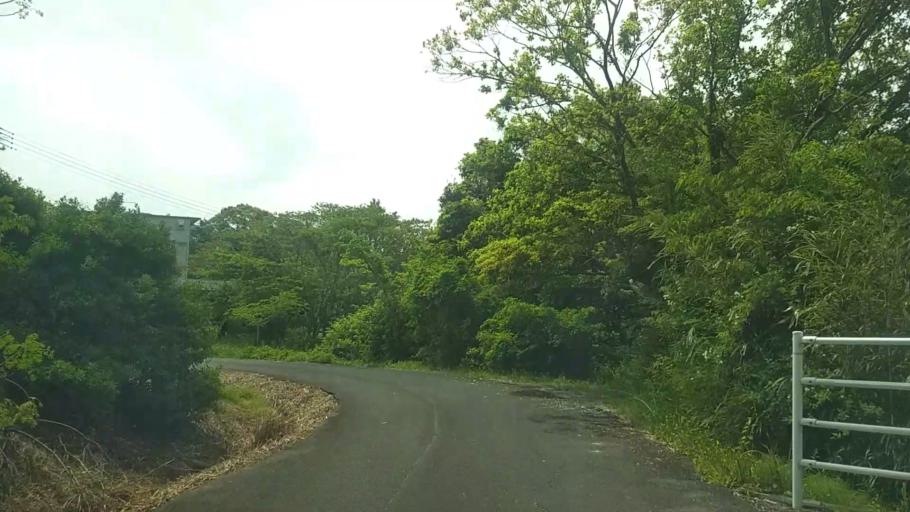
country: JP
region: Shizuoka
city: Kosai-shi
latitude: 34.7541
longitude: 137.5287
